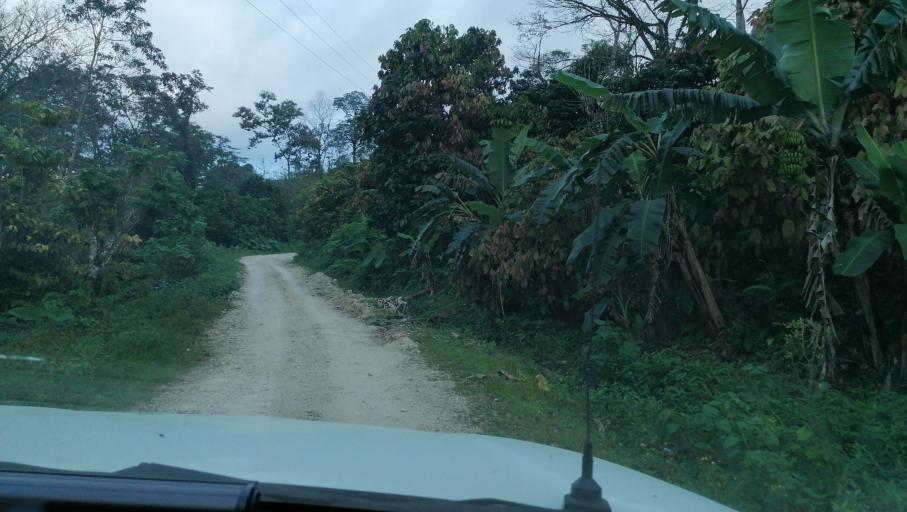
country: MX
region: Chiapas
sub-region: Francisco Leon
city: San Miguel la Sardina
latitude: 17.3079
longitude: -93.2681
